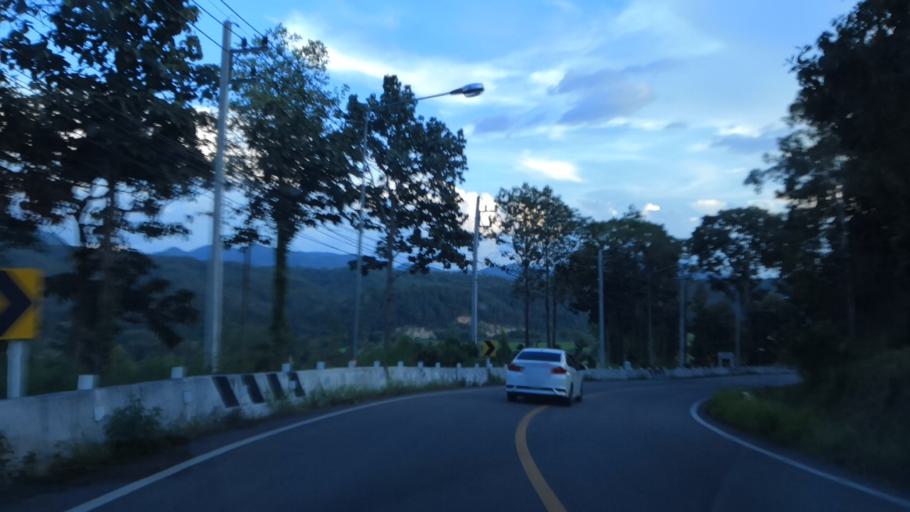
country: TH
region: Mae Hong Son
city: Khun Yuam
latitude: 18.7462
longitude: 97.9273
